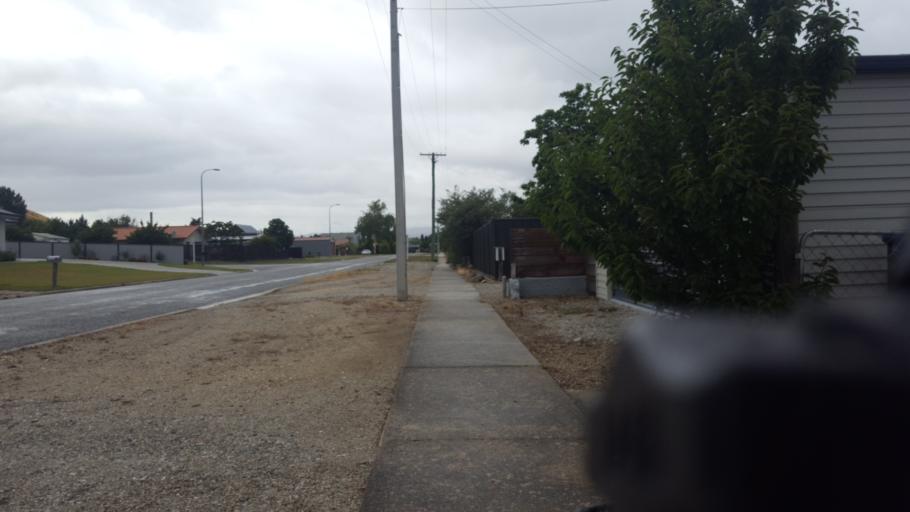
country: NZ
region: Otago
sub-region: Queenstown-Lakes District
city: Wanaka
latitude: -45.1893
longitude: 169.3279
